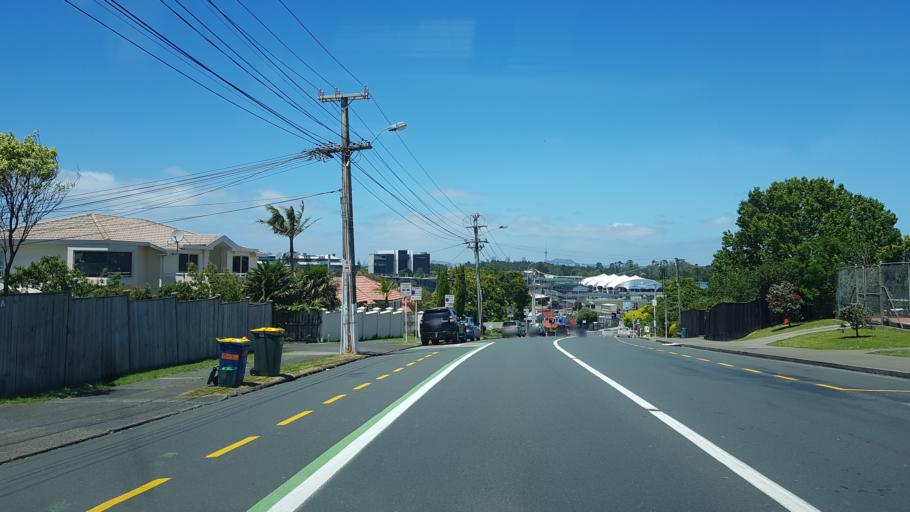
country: NZ
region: Auckland
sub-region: Auckland
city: North Shore
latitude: -36.7778
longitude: 174.7500
